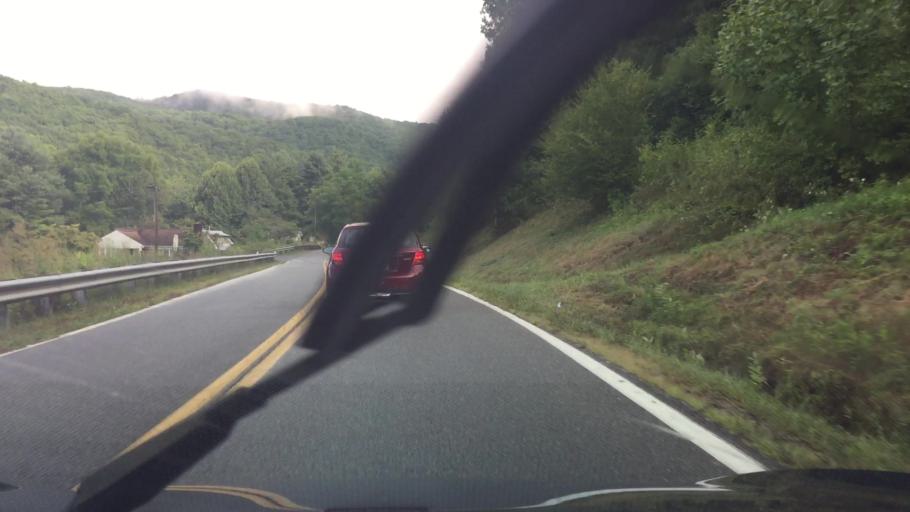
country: US
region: Virginia
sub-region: Smyth County
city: Atkins
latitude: 36.8419
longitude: -81.4232
